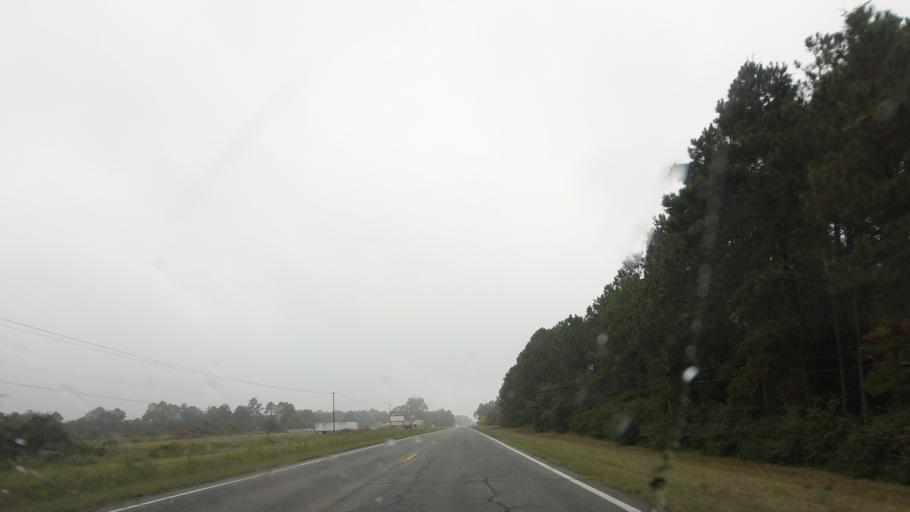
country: US
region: Georgia
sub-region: Ben Hill County
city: Fitzgerald
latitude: 31.7405
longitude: -83.2462
